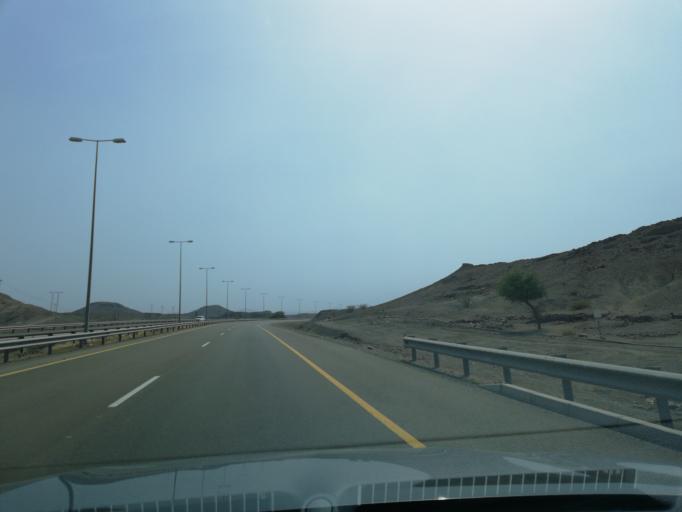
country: OM
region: Al Batinah
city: Al Liwa'
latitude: 24.3214
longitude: 56.4688
